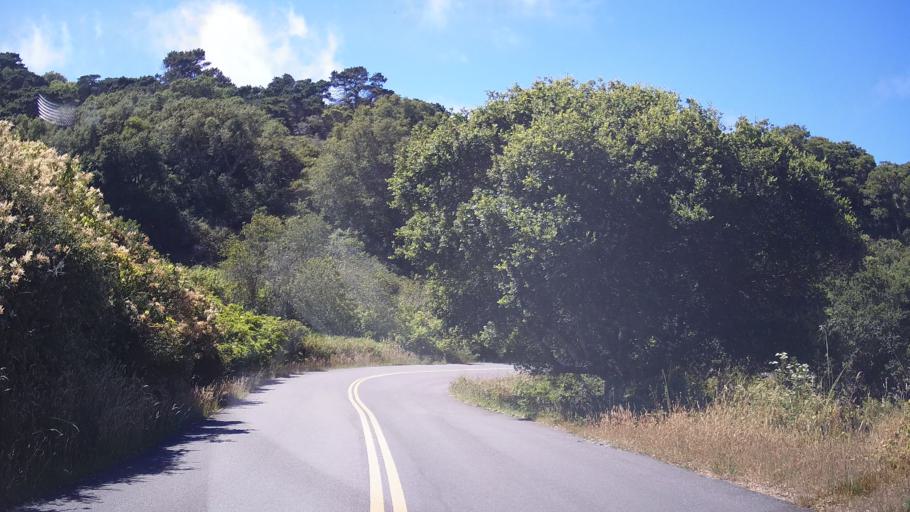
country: US
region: California
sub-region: Marin County
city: Inverness
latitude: 38.1269
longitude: -122.9025
